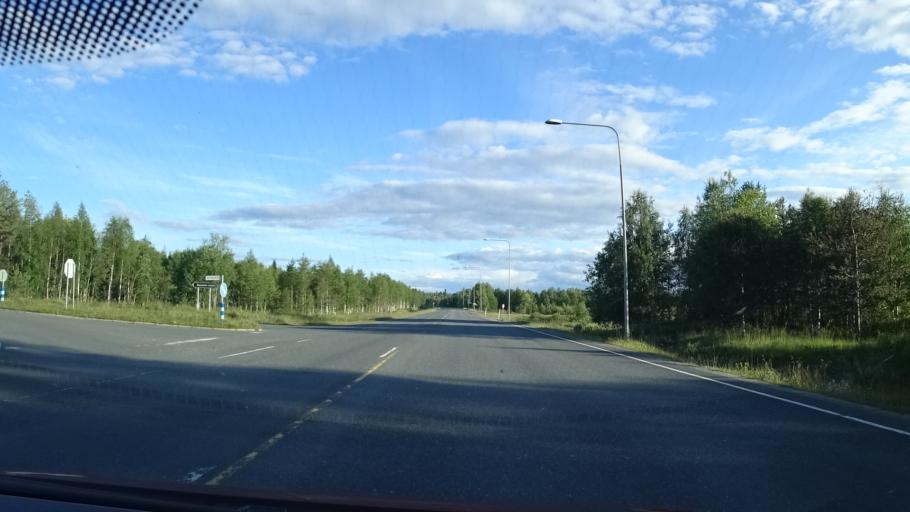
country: FI
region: Northern Ostrobothnia
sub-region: Koillismaa
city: Kuusamo
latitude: 66.0002
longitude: 29.1514
